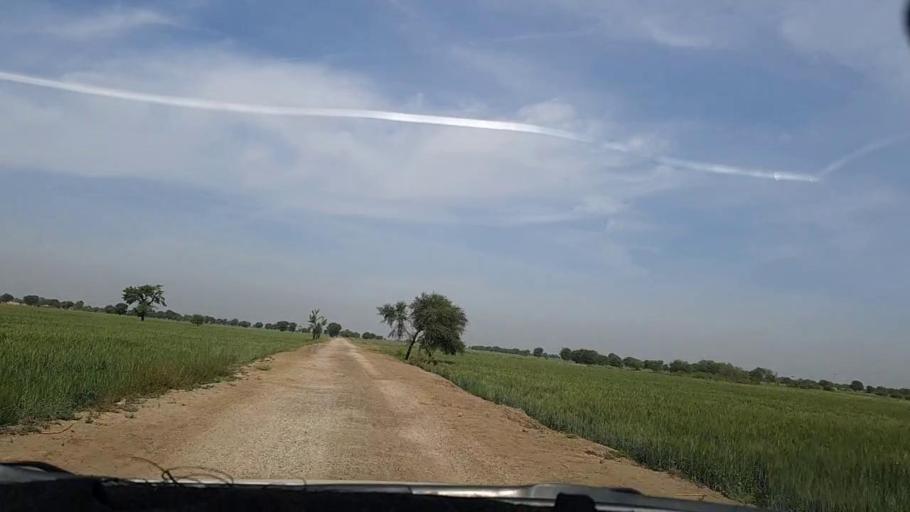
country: PK
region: Sindh
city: Dhoro Naro
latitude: 25.4440
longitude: 69.4971
